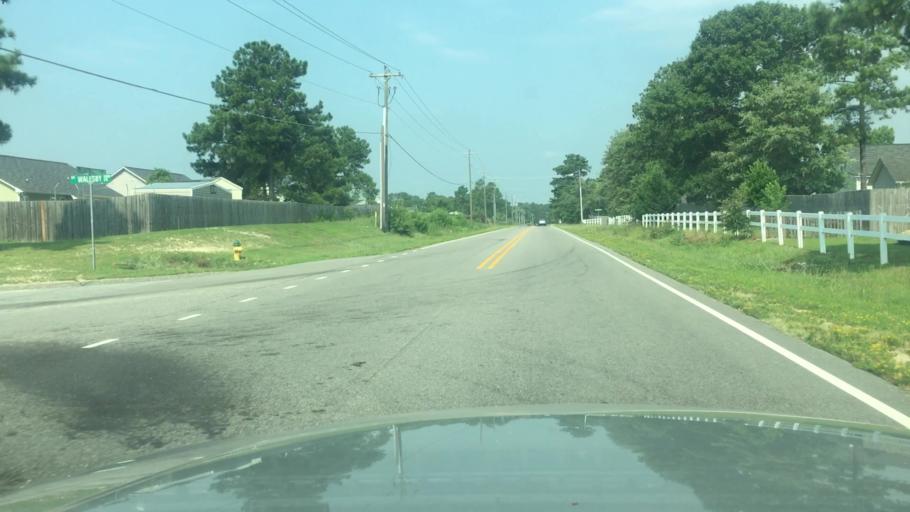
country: US
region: North Carolina
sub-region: Cumberland County
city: Hope Mills
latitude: 35.0000
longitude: -78.9453
